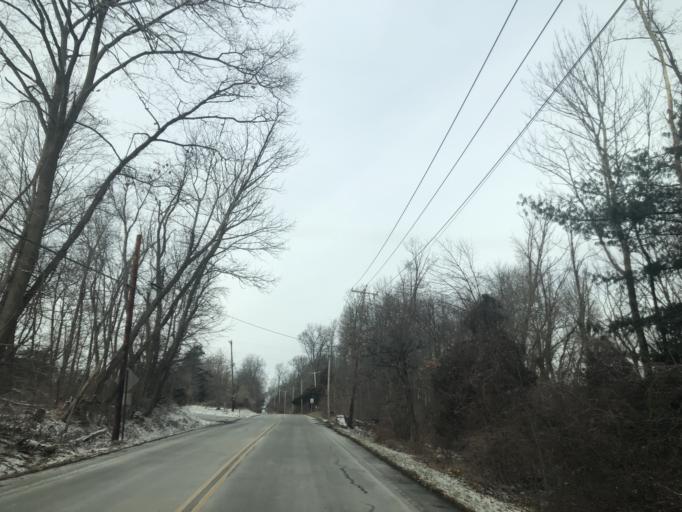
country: US
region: New Jersey
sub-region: Warren County
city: Belvidere
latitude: 40.9299
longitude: -75.0044
